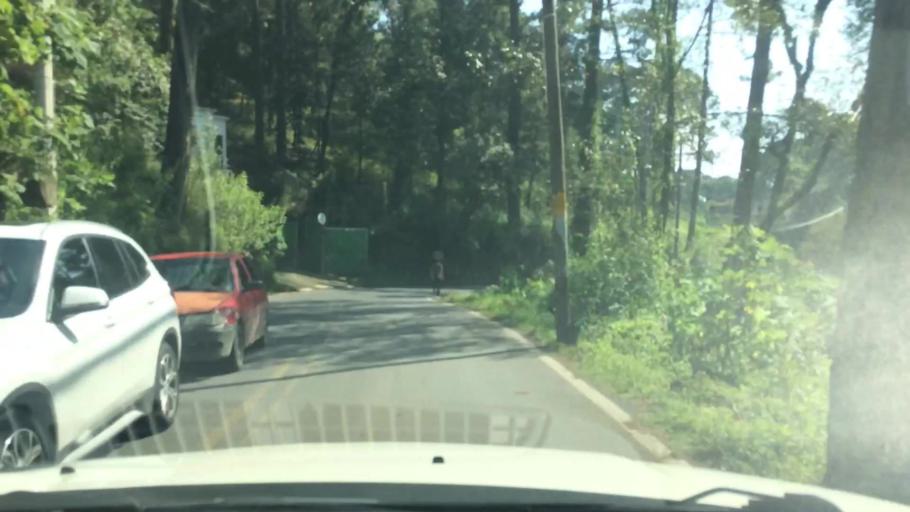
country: MX
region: Mexico
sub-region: Valle de Bravo
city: Casas Viejas
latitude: 19.1736
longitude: -100.1122
